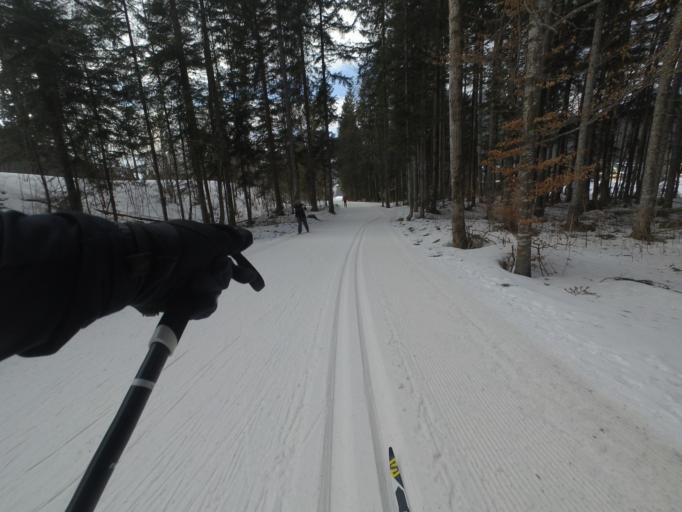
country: AT
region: Salzburg
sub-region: Politischer Bezirk Salzburg-Umgebung
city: Fuschl am See
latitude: 47.7733
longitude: 13.3028
